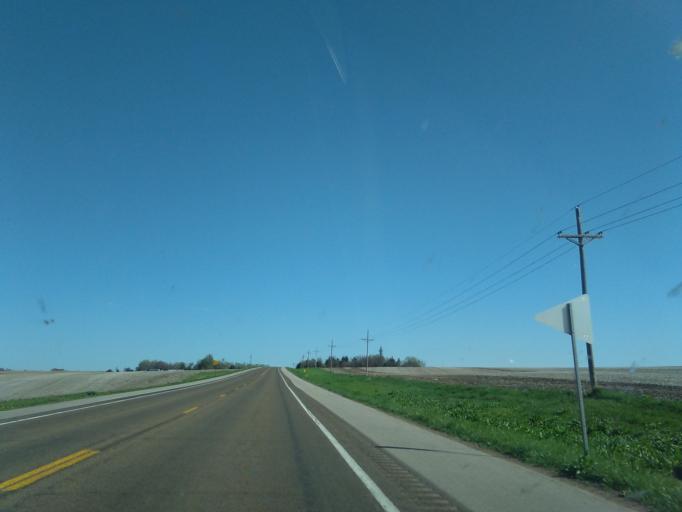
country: US
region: Nebraska
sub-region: Dodge County
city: Fremont
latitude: 41.3508
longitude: -96.5021
